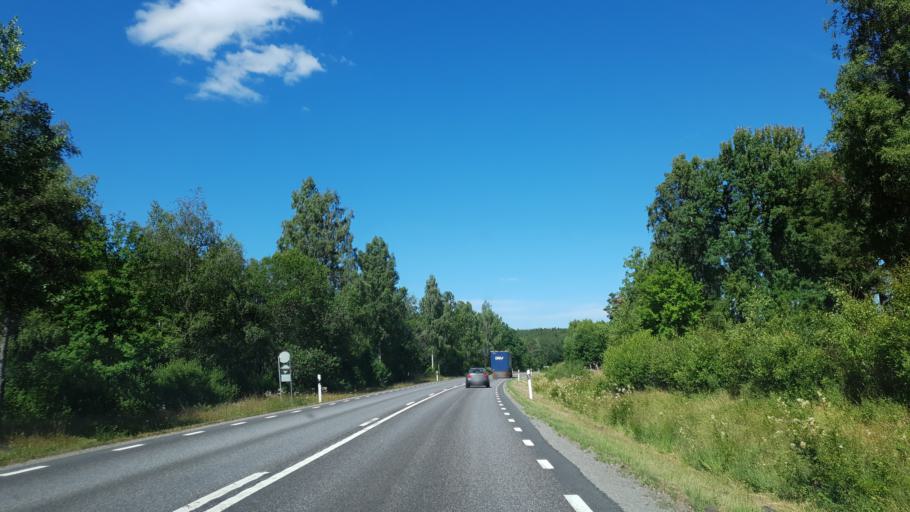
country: SE
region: Joenkoeping
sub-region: Varnamo Kommun
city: Rydaholm
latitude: 57.0036
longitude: 14.2681
